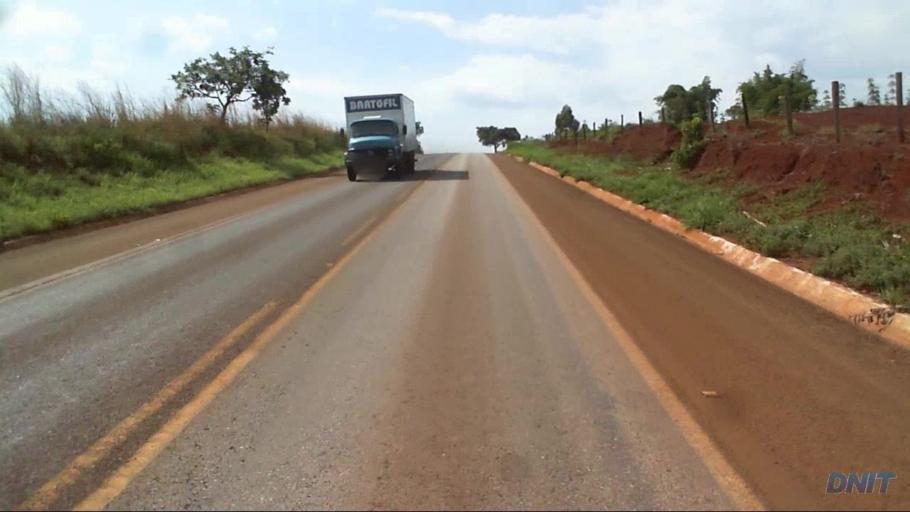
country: BR
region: Goias
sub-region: Barro Alto
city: Barro Alto
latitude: -14.9984
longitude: -48.9056
